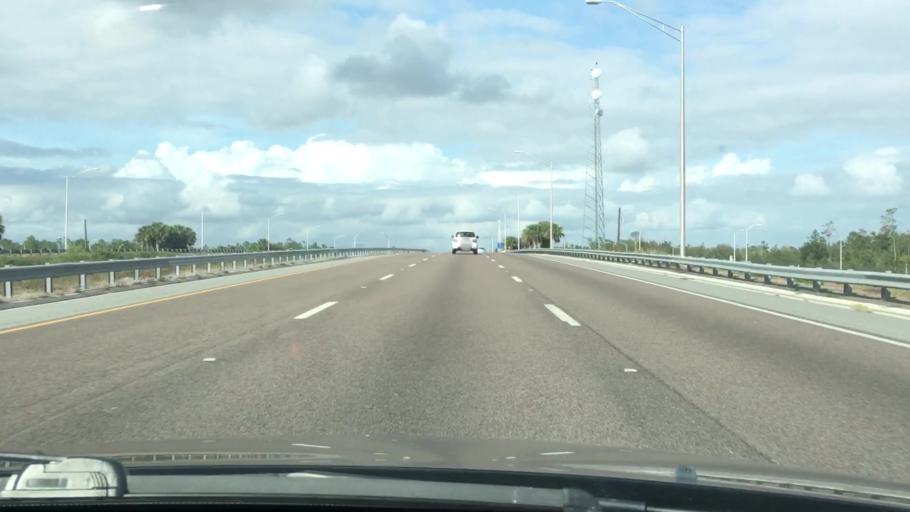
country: US
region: Florida
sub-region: Volusia County
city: Edgewater
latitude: 28.9491
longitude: -80.9496
